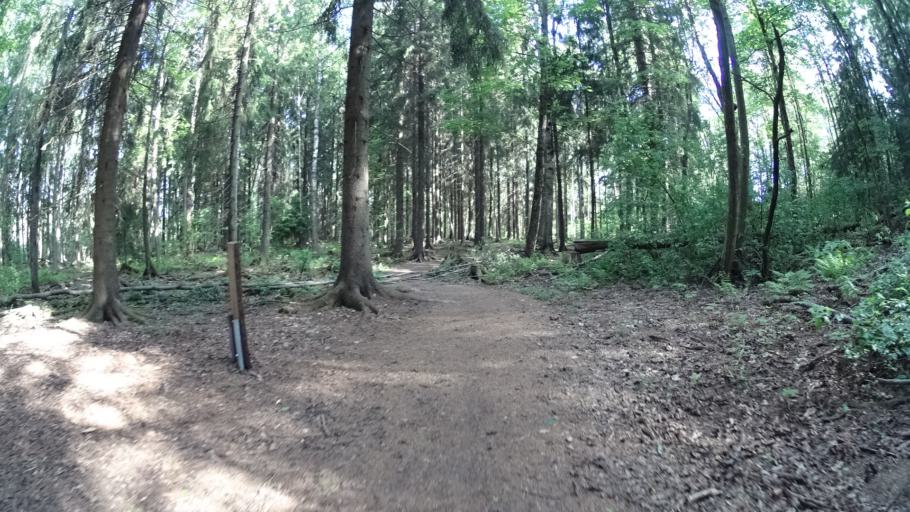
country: FI
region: Uusimaa
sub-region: Helsinki
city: Kilo
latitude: 60.2644
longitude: 24.7897
